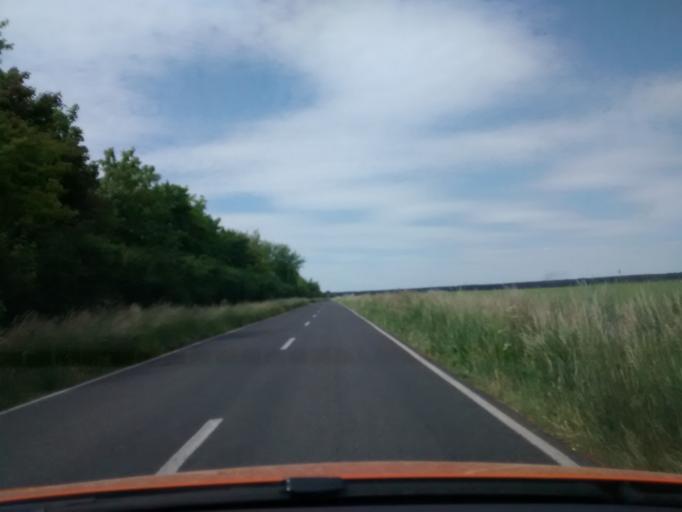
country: DE
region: Brandenburg
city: Ihlow
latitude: 51.9375
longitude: 13.3357
